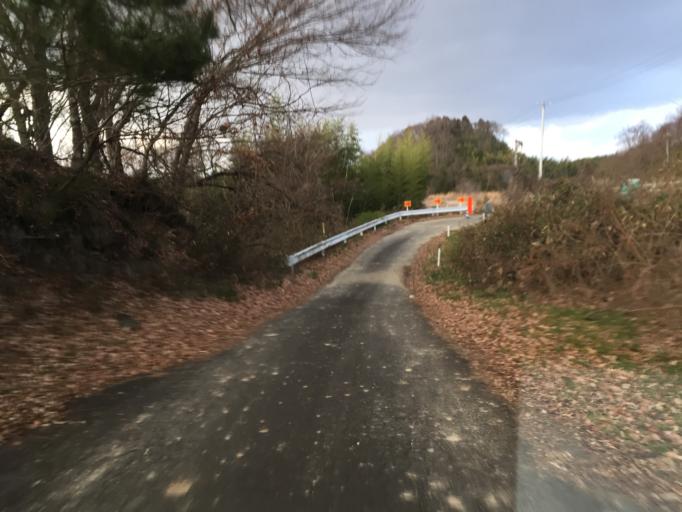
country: JP
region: Fukushima
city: Nihommatsu
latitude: 37.5592
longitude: 140.4406
